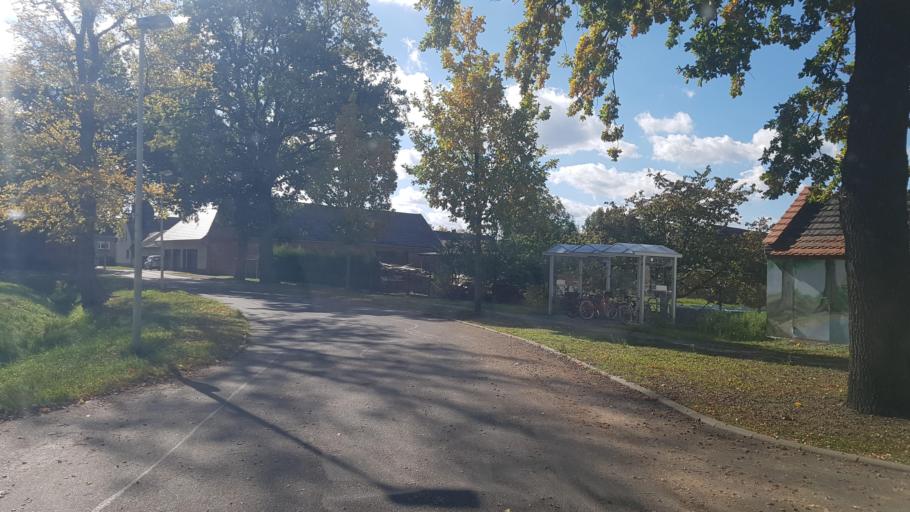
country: DE
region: Brandenburg
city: Cottbus
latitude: 51.8045
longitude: 14.3538
